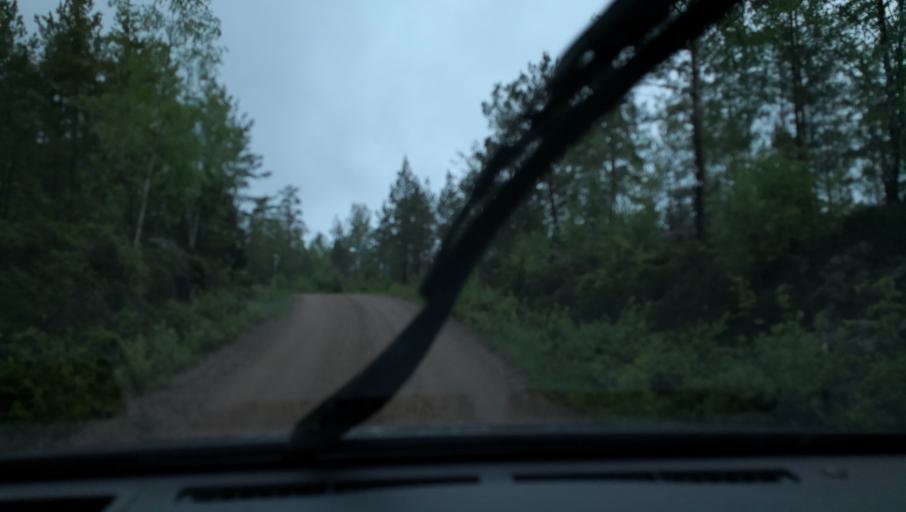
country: SE
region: Uppsala
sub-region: Enkopings Kommun
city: Orsundsbro
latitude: 59.9325
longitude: 17.3278
